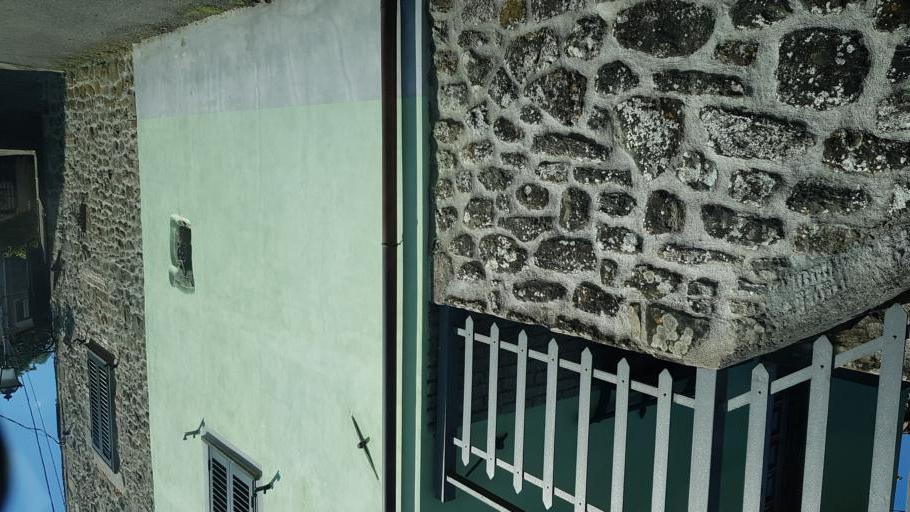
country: IT
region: Tuscany
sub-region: Provincia di Lucca
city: San Romano
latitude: 44.1800
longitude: 10.3344
